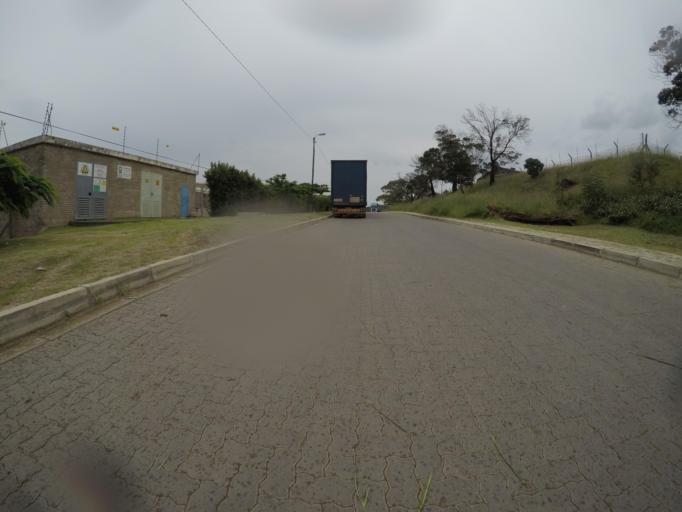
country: ZA
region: Eastern Cape
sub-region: Buffalo City Metropolitan Municipality
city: East London
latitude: -32.9895
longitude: 27.8295
